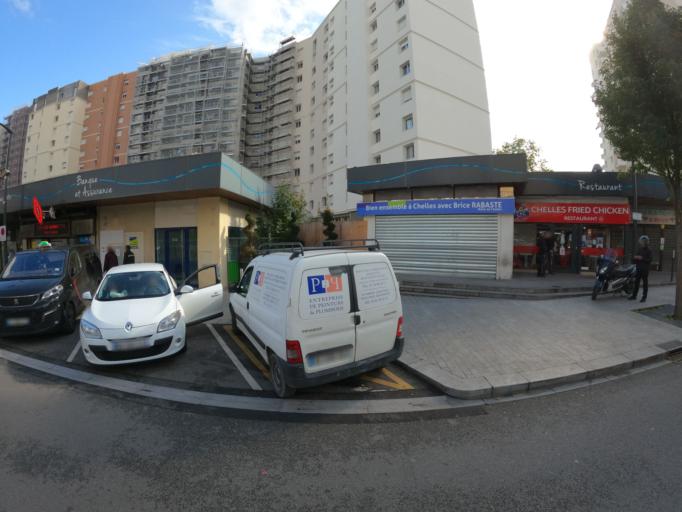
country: FR
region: Ile-de-France
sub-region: Departement de Seine-et-Marne
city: Chelles
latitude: 48.8786
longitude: 2.5921
